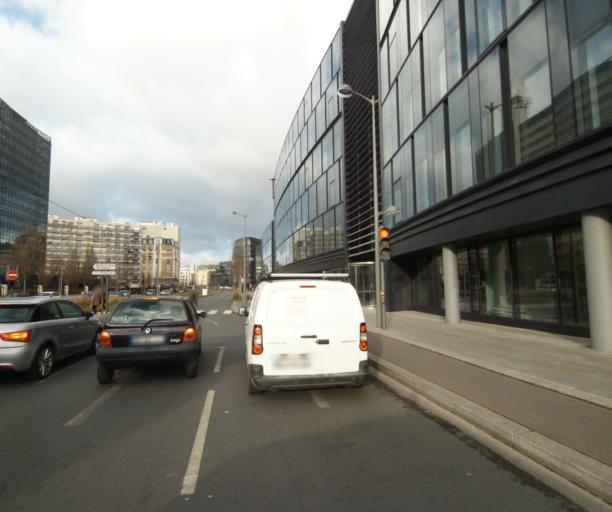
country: FR
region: Ile-de-France
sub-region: Departement des Hauts-de-Seine
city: La Garenne-Colombes
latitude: 48.9049
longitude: 2.2394
